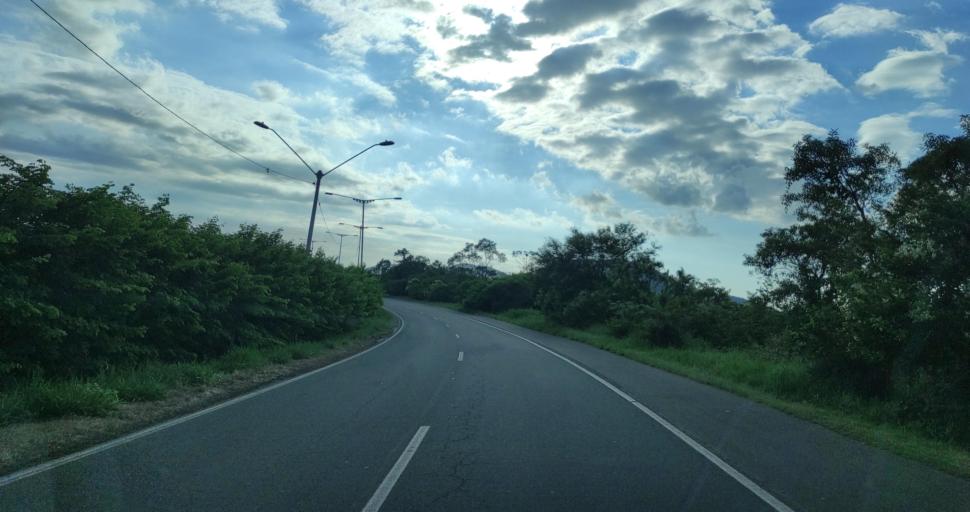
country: BR
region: Santa Catarina
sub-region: Penha
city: Penha
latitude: -26.8060
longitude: -48.6411
